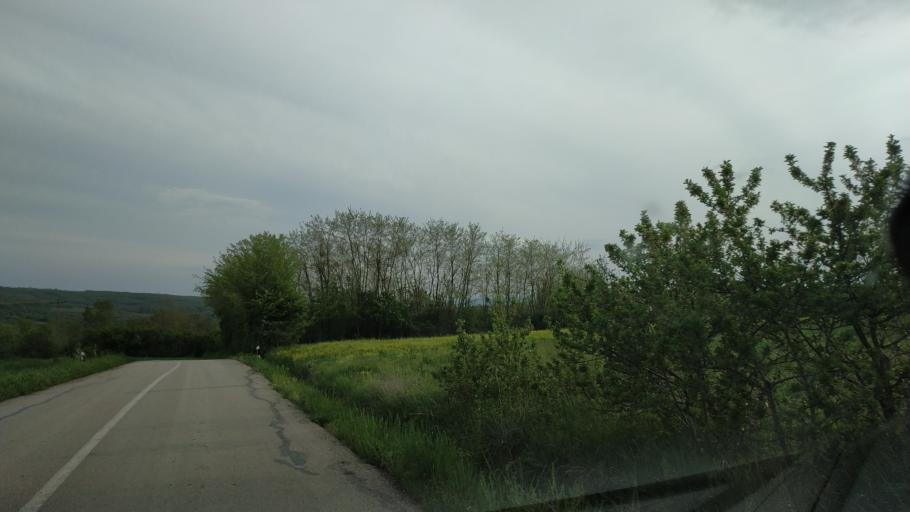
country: RS
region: Central Serbia
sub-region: Zajecarski Okrug
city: Soko Banja
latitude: 43.5210
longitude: 21.8479
